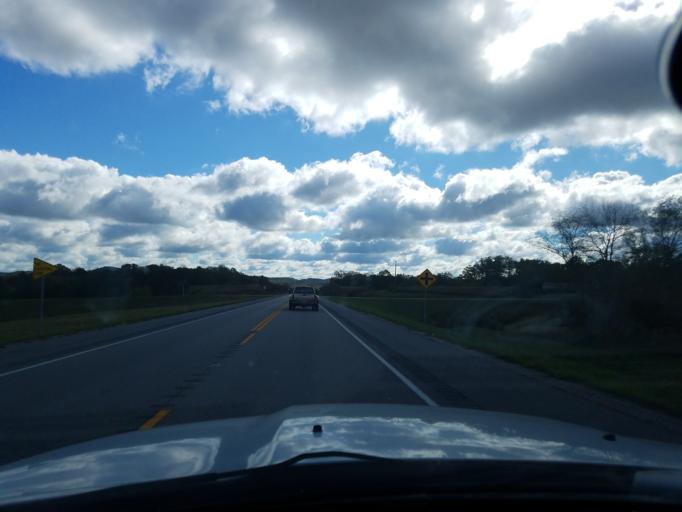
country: US
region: Kentucky
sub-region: Rockcastle County
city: Brodhead
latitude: 37.4463
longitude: -84.4830
